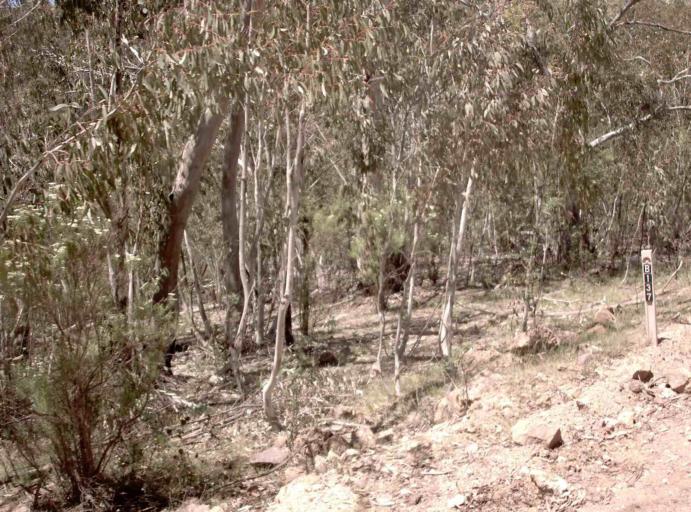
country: AU
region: New South Wales
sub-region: Snowy River
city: Jindabyne
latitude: -37.0603
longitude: 148.3076
